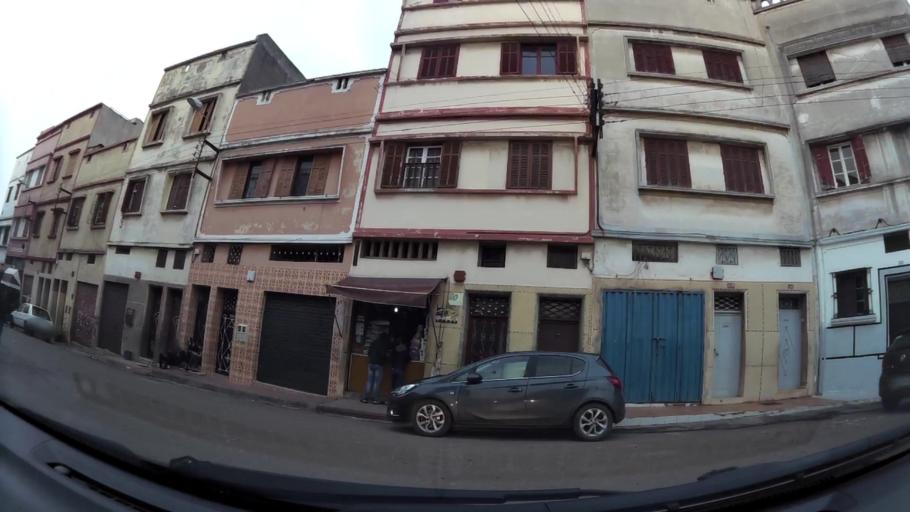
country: MA
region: Grand Casablanca
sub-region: Casablanca
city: Casablanca
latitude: 33.5560
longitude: -7.5986
